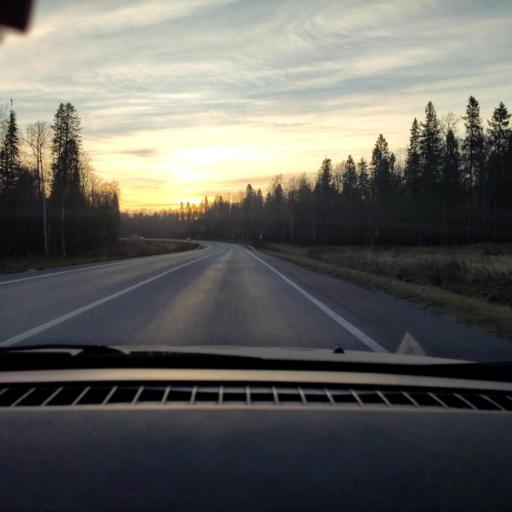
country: RU
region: Perm
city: Novyye Lyady
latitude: 58.0276
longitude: 56.5055
